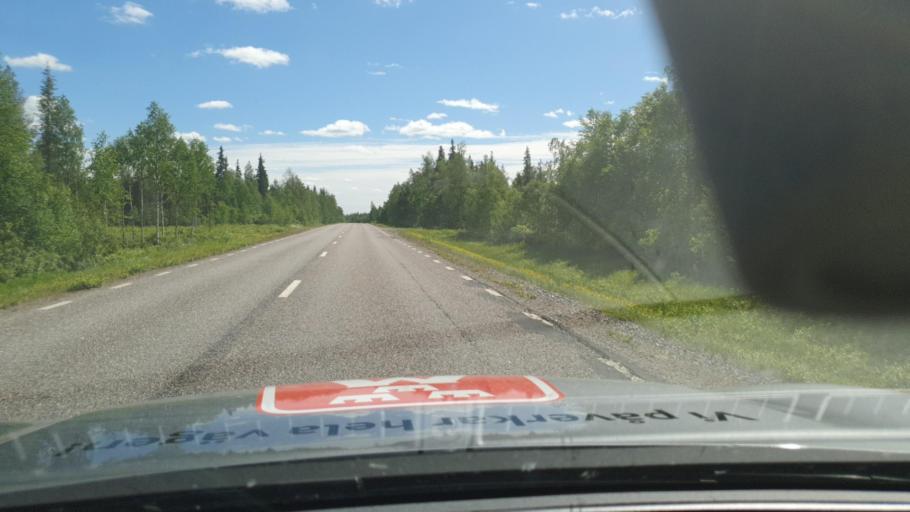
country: SE
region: Norrbotten
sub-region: Pajala Kommun
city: Pajala
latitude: 67.1258
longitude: 23.5961
